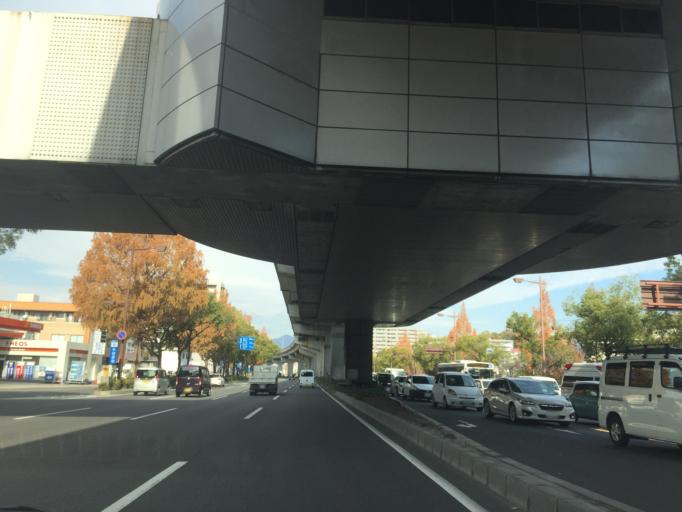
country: JP
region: Hiroshima
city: Hiroshima-shi
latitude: 34.4169
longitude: 132.4645
